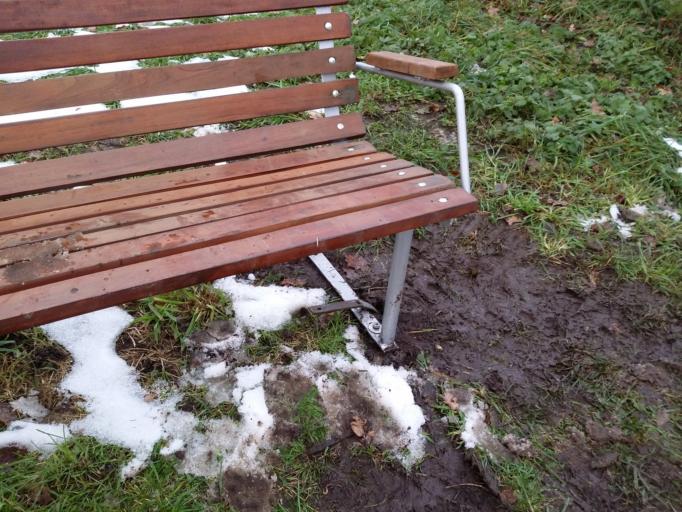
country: DK
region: Capital Region
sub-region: Frederikssund Kommune
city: Skibby
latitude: 55.7553
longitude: 11.9620
